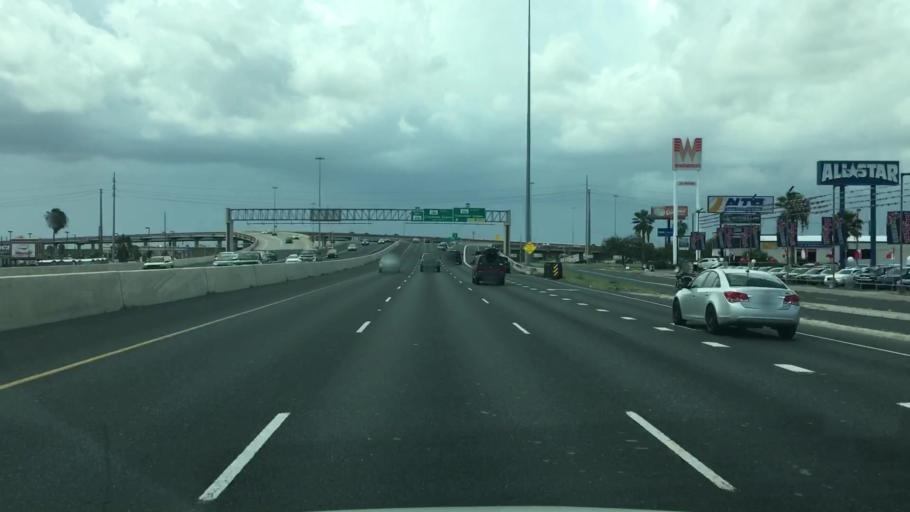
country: US
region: Texas
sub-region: Nueces County
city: Corpus Christi
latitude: 27.7344
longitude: -97.4247
